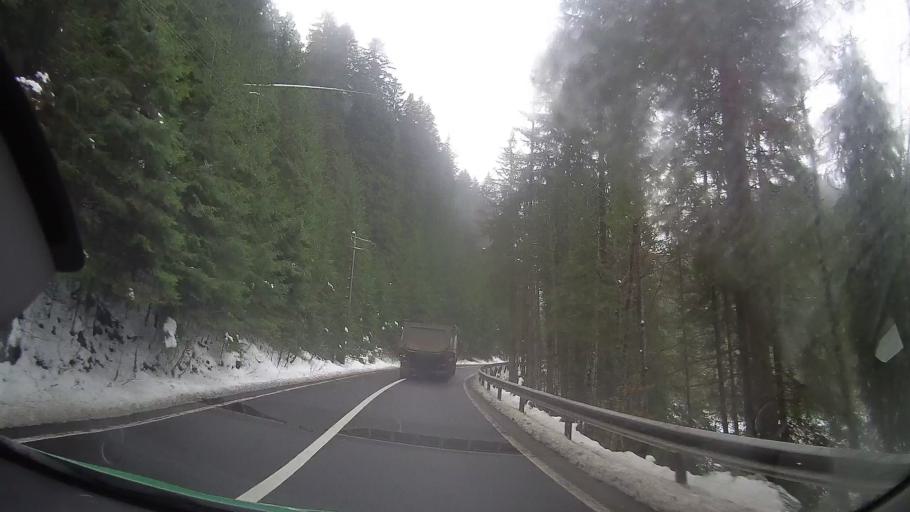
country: RO
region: Neamt
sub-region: Comuna Bicaz Chei
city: Bicaz Chei
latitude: 46.7815
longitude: 25.7823
